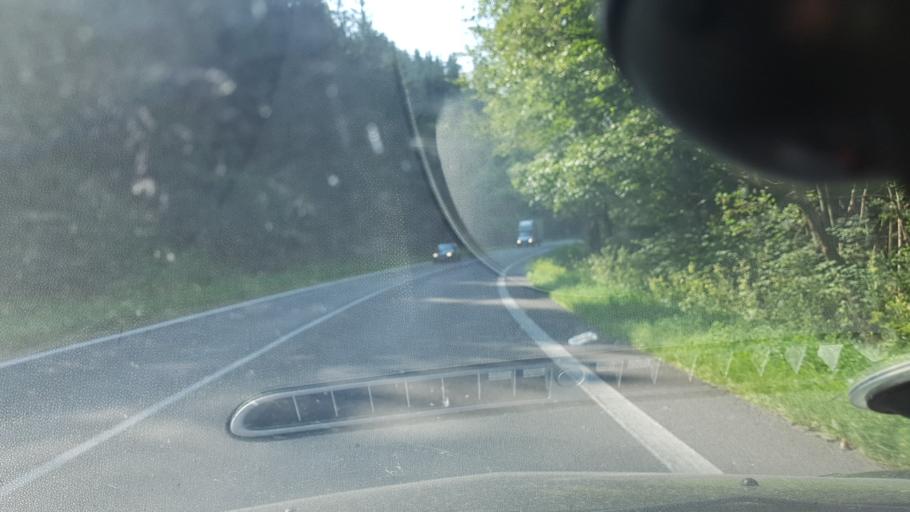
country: SK
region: Zilinsky
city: Ruzomberok
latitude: 49.1347
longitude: 19.2887
